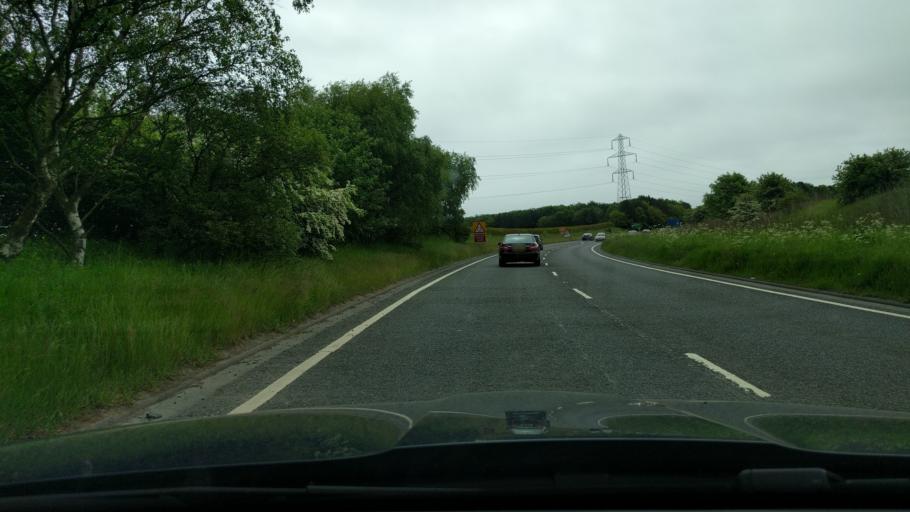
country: GB
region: England
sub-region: Northumberland
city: Lynemouth
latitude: 55.1933
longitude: -1.5407
